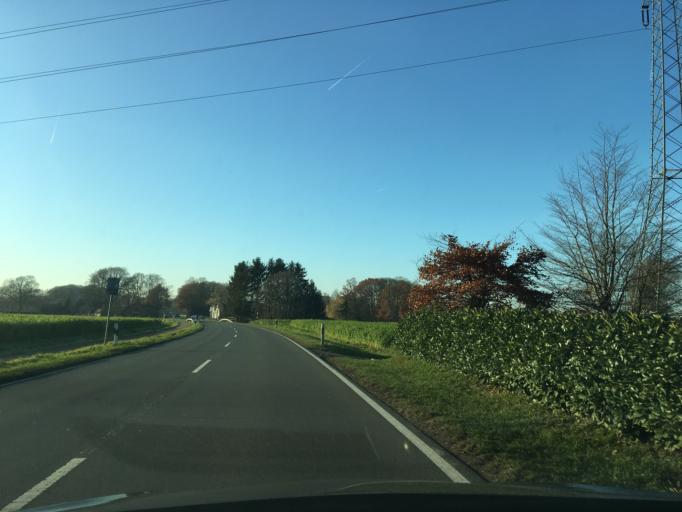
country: DE
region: North Rhine-Westphalia
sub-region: Regierungsbezirk Munster
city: Ahaus
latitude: 52.1190
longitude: 6.9327
